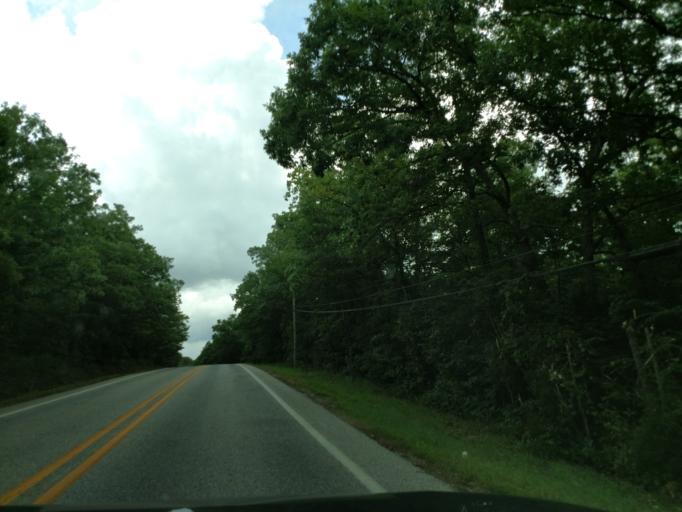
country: US
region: Arkansas
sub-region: Boone County
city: Harrison
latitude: 36.2403
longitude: -93.2119
